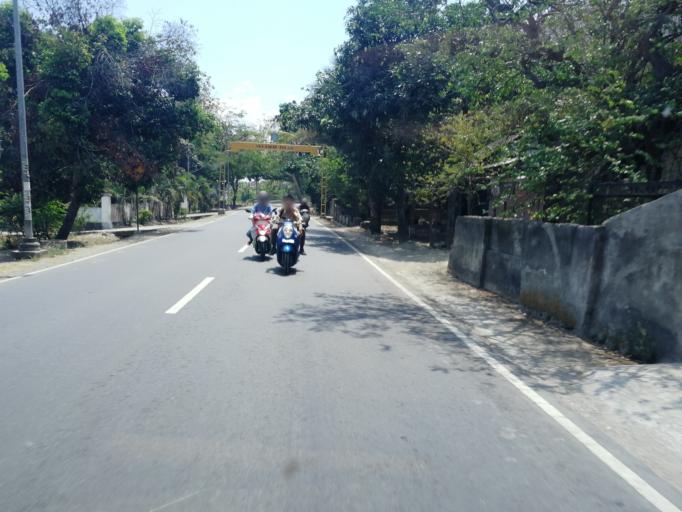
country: ID
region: West Nusa Tenggara
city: Jelateng Timur
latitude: -8.7075
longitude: 116.0805
